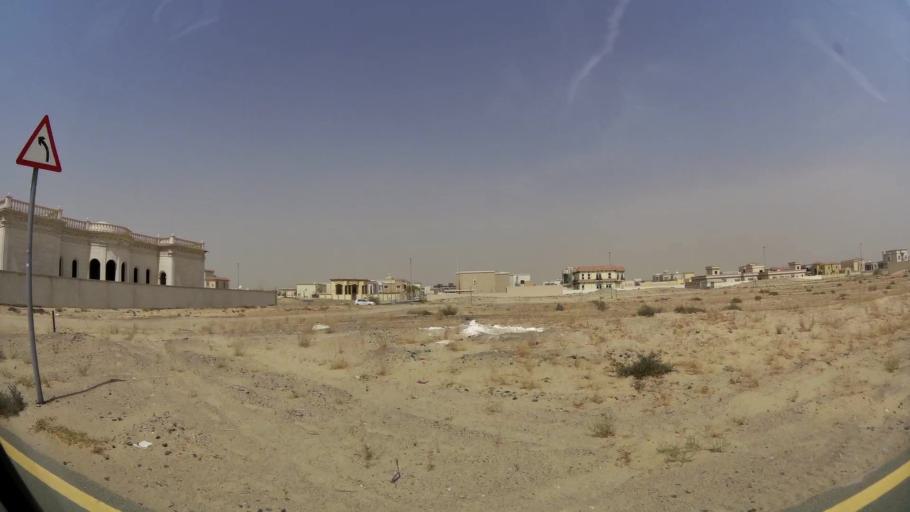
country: AE
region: Ash Shariqah
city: Sharjah
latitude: 25.2557
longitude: 55.4859
